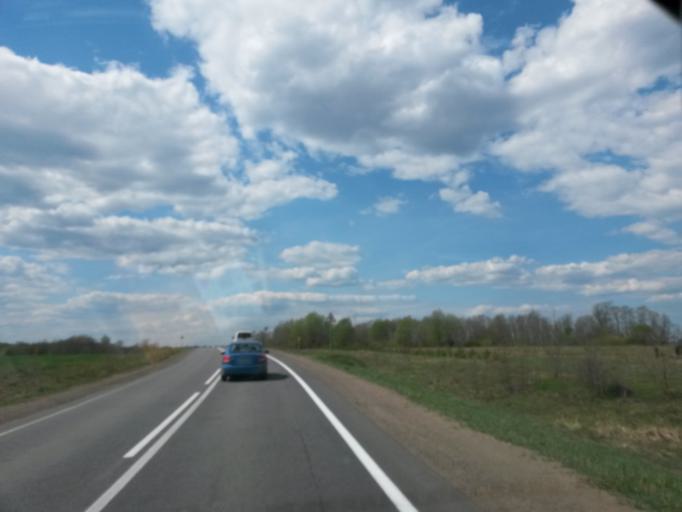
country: RU
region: Jaroslavl
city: Bol'shoye Selo
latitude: 57.7270
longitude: 38.9088
